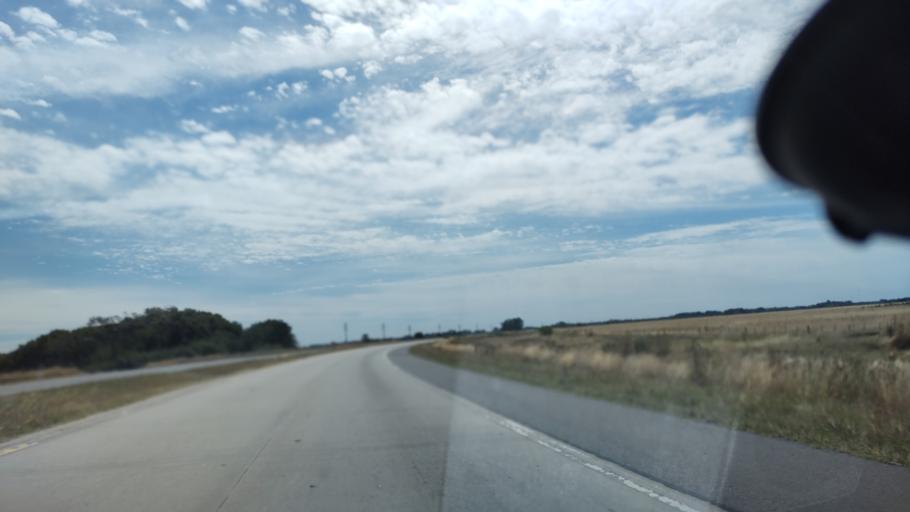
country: AR
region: Buenos Aires
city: Canuelas
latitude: -35.0762
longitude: -58.6874
